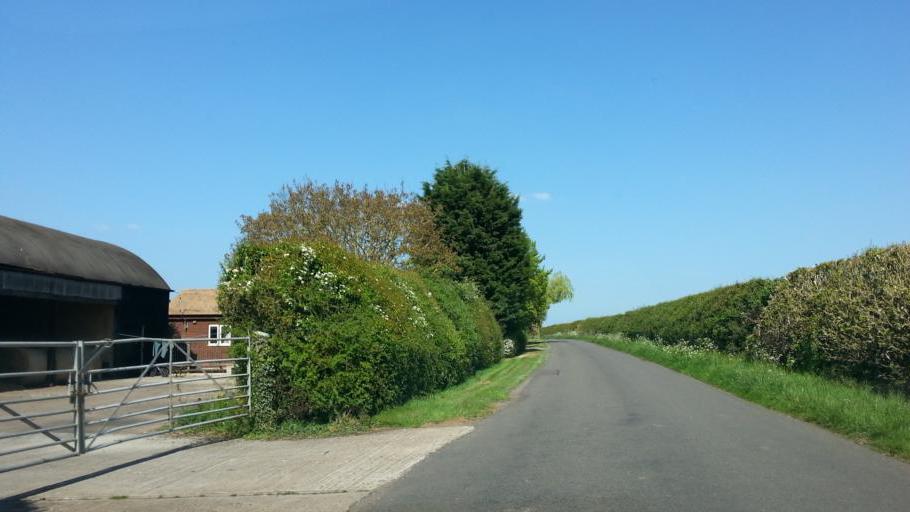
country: GB
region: England
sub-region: Nottinghamshire
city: Farndon
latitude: 52.9884
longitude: -0.8509
